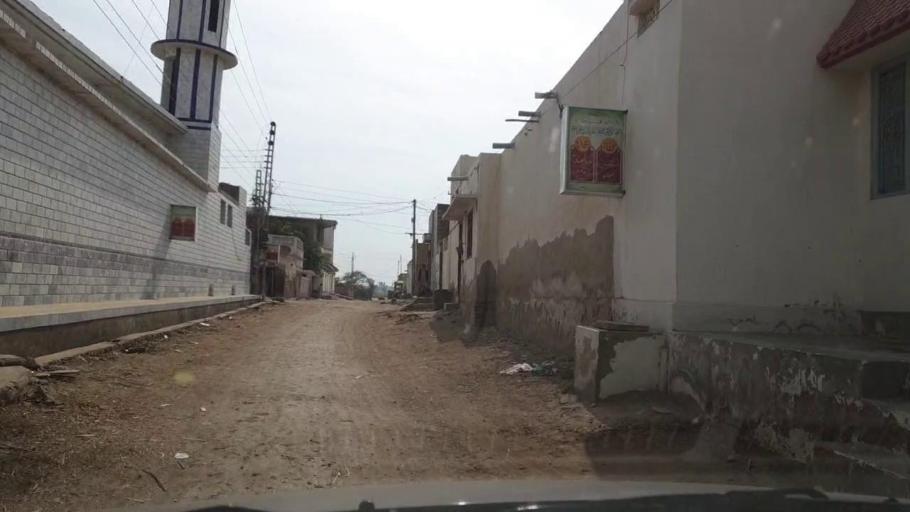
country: PK
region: Sindh
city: Sinjhoro
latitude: 26.1053
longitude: 68.8286
